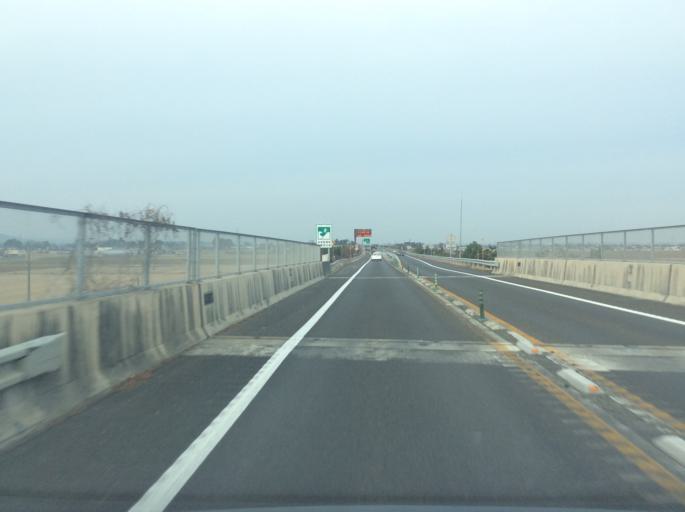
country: JP
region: Miyagi
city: Iwanuma
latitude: 38.0995
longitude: 140.8888
